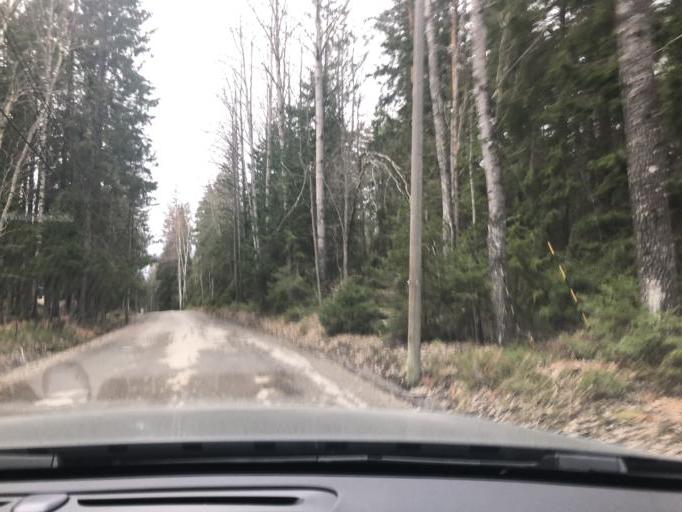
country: SE
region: Stockholm
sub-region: Huddinge Kommun
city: Segeltorp
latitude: 59.2471
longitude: 17.9288
